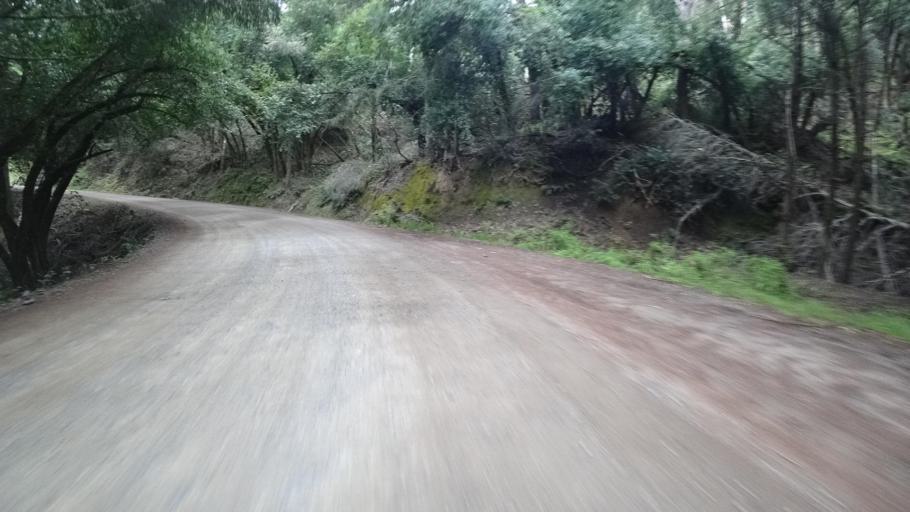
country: US
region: California
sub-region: Humboldt County
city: Redway
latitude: 40.2667
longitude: -123.7693
